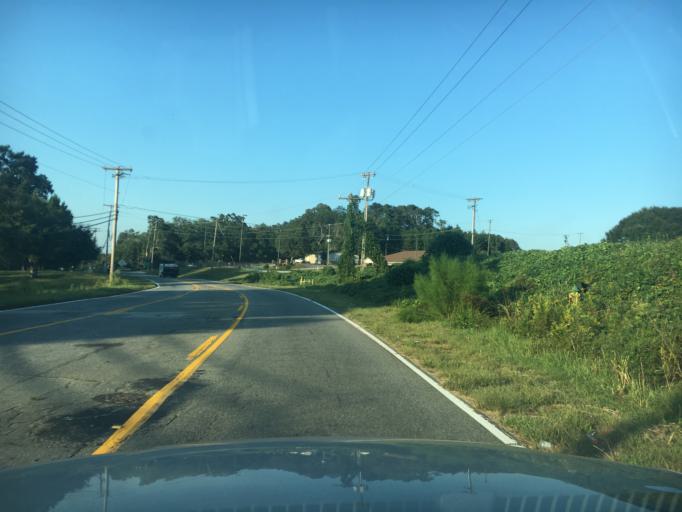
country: US
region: South Carolina
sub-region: Greenville County
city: Greer
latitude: 34.9488
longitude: -82.2132
